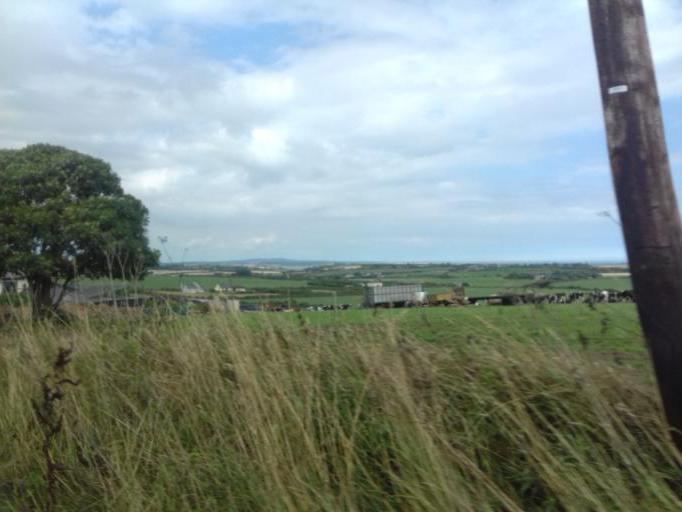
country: IE
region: Munster
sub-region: Waterford
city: Dunmore East
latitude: 52.1721
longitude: -6.8796
